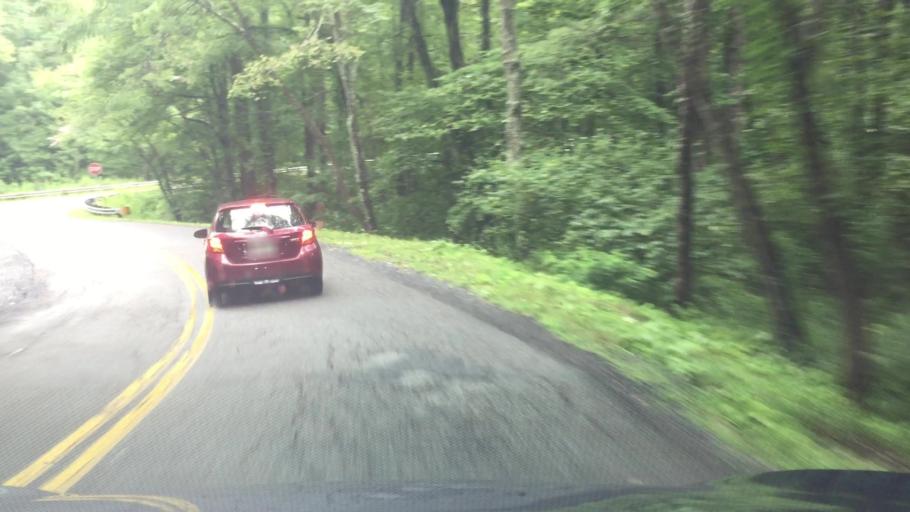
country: US
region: Virginia
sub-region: Smyth County
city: Atkins
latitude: 36.8115
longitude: -81.4086
